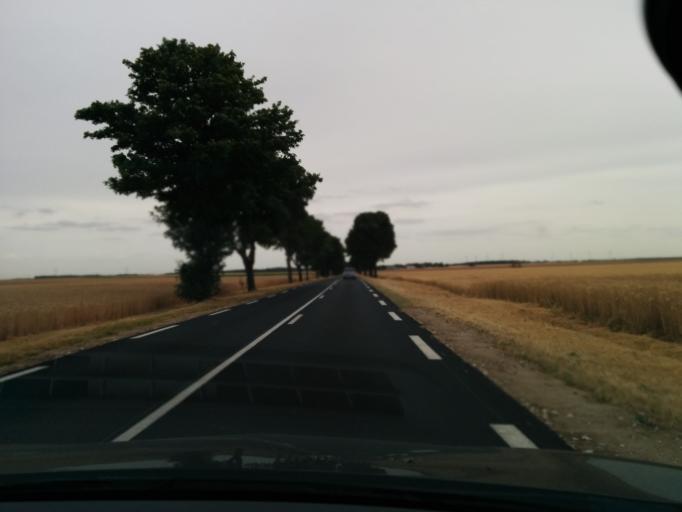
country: FR
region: Ile-de-France
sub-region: Departement de l'Essonne
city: Pussay
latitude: 48.3892
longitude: 1.9743
